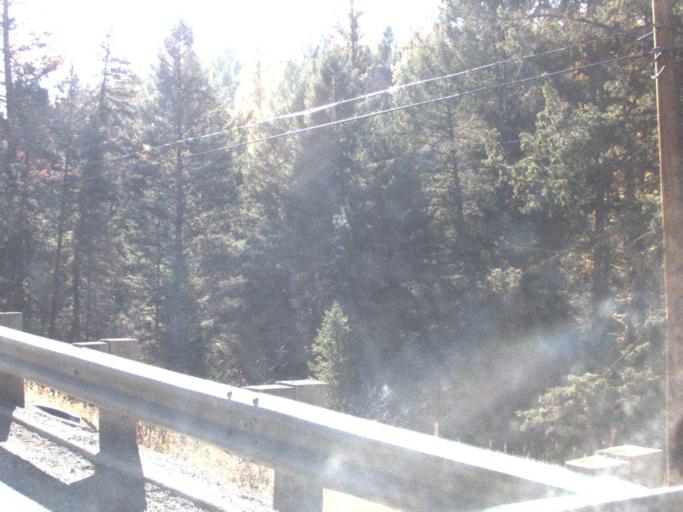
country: US
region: Washington
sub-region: Ferry County
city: Republic
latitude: 48.6407
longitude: -118.6813
